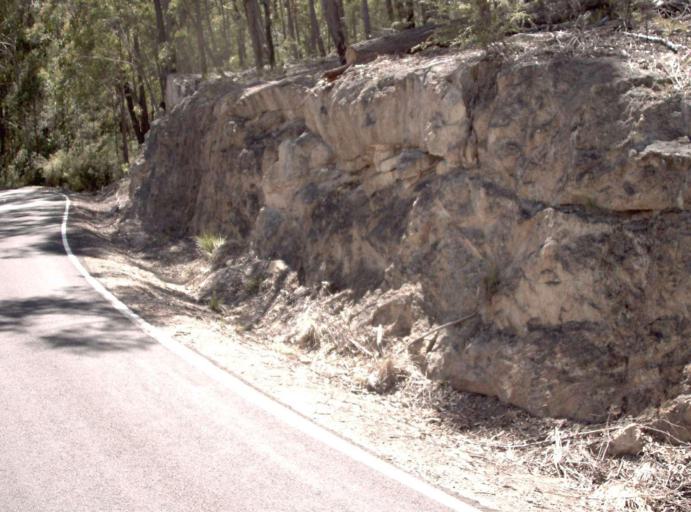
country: AU
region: Victoria
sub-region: East Gippsland
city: Lakes Entrance
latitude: -37.3706
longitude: 148.2194
